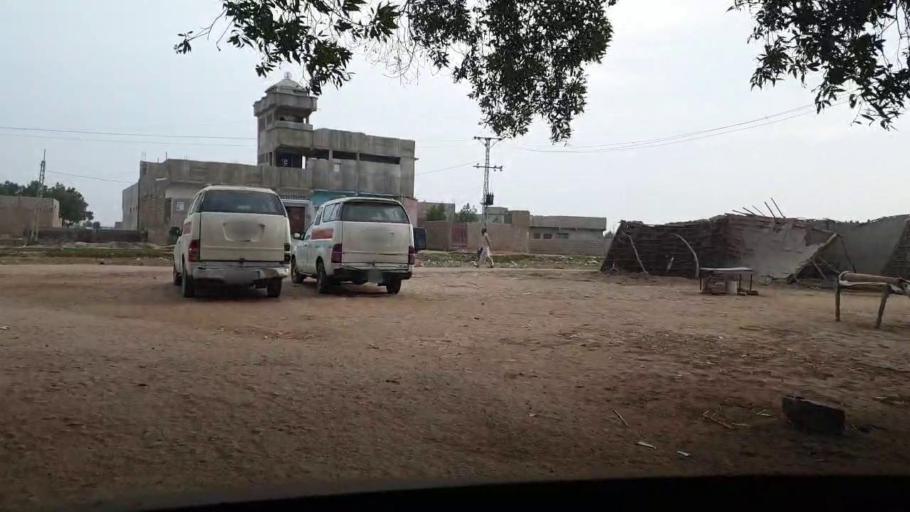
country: PK
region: Sindh
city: Thatta
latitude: 24.5989
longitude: 68.0822
